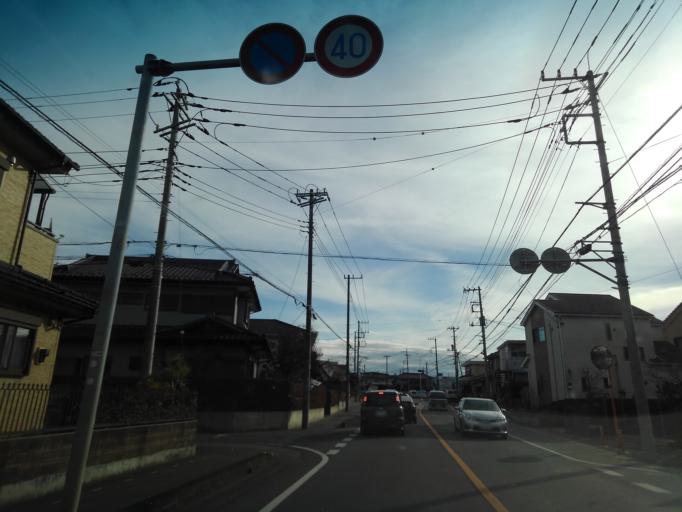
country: JP
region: Saitama
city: Morohongo
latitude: 35.8999
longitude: 139.3348
